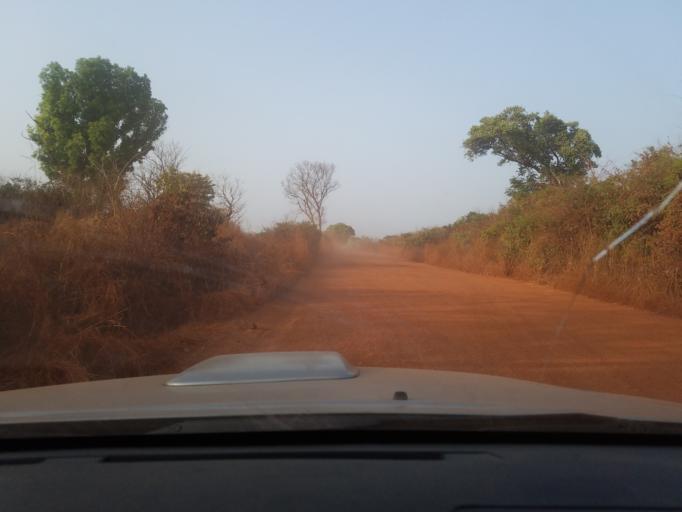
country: GN
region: Boke
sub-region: Gaoual Prefecture
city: Gaoual
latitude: 11.5037
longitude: -13.8602
